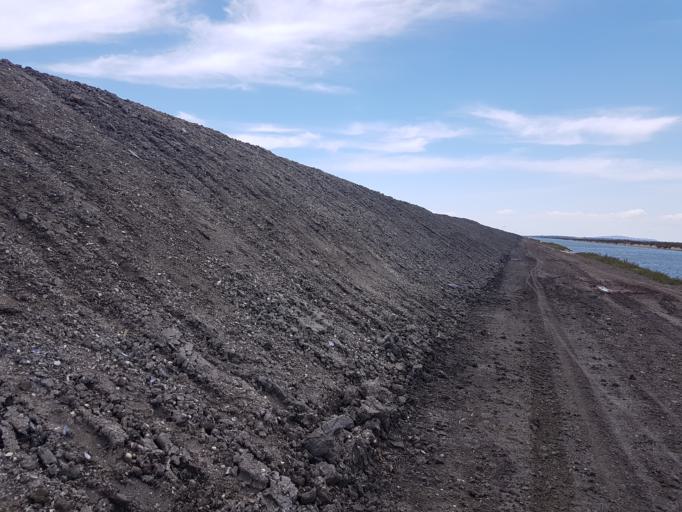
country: FR
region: Languedoc-Roussillon
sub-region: Departement de l'Herault
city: Villeneuve-les-Maguelone
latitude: 43.5070
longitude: 3.8675
